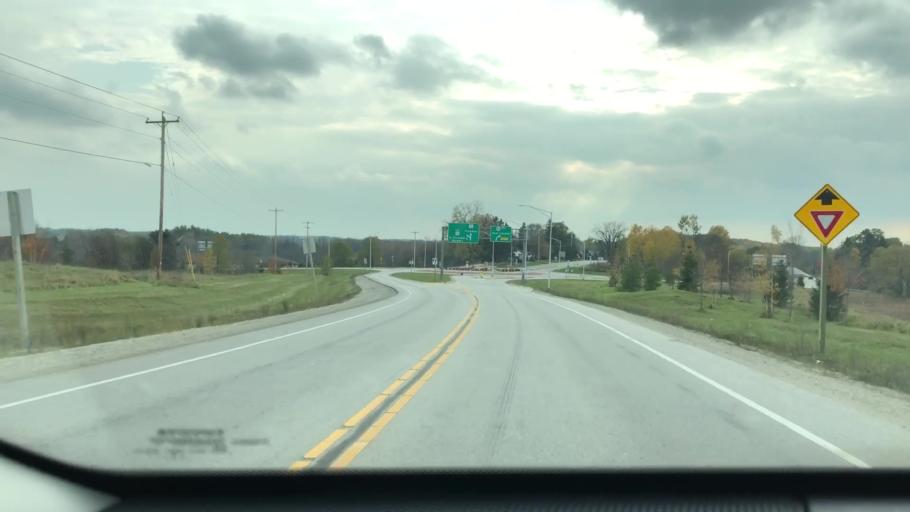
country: US
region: Wisconsin
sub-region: Brown County
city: Oneida
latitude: 44.5019
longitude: -88.1753
